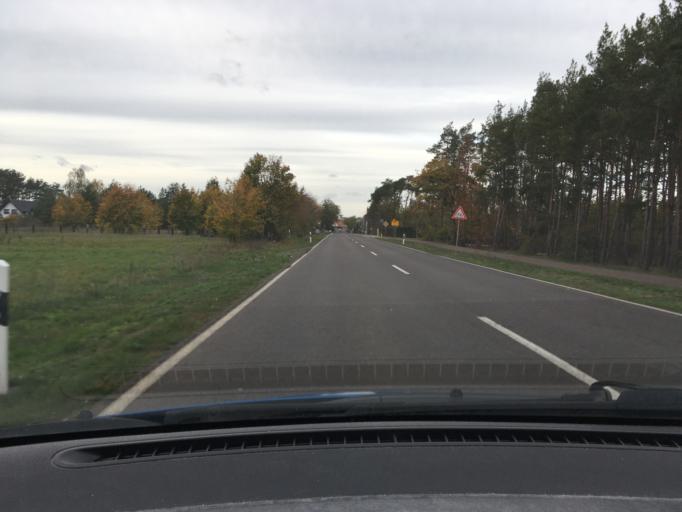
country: DE
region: Saxony-Anhalt
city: Wahlitz
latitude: 52.1018
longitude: 11.7833
